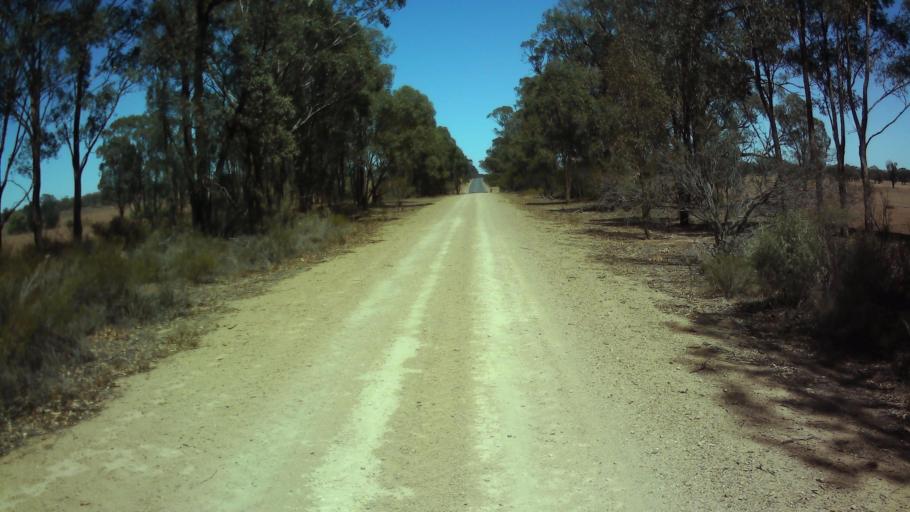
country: AU
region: New South Wales
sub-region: Forbes
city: Forbes
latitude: -33.6939
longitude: 147.8114
